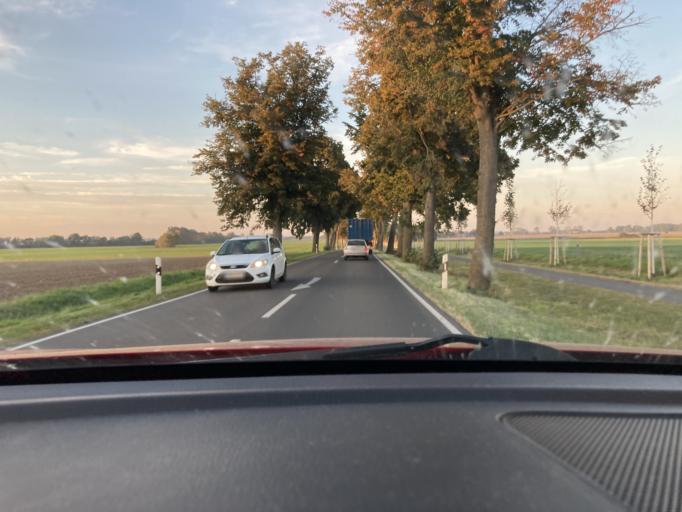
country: DE
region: Mecklenburg-Vorpommern
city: Anklam
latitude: 53.7919
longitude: 13.6650
